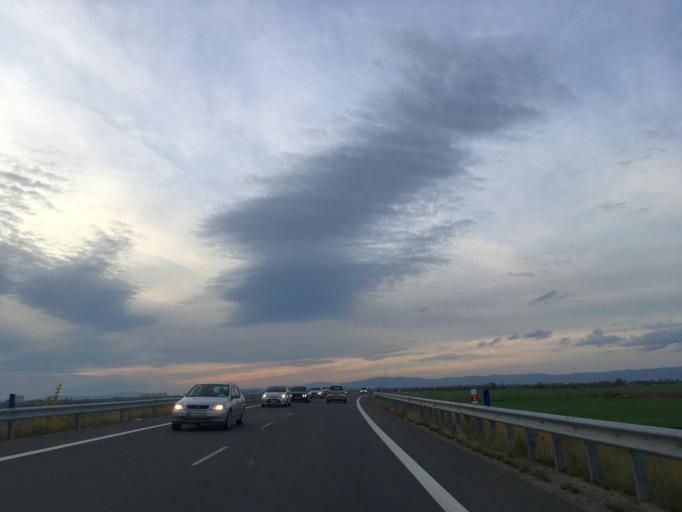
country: SK
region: Bratislavsky
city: Dunajska Luzna
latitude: 48.1284
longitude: 17.2698
